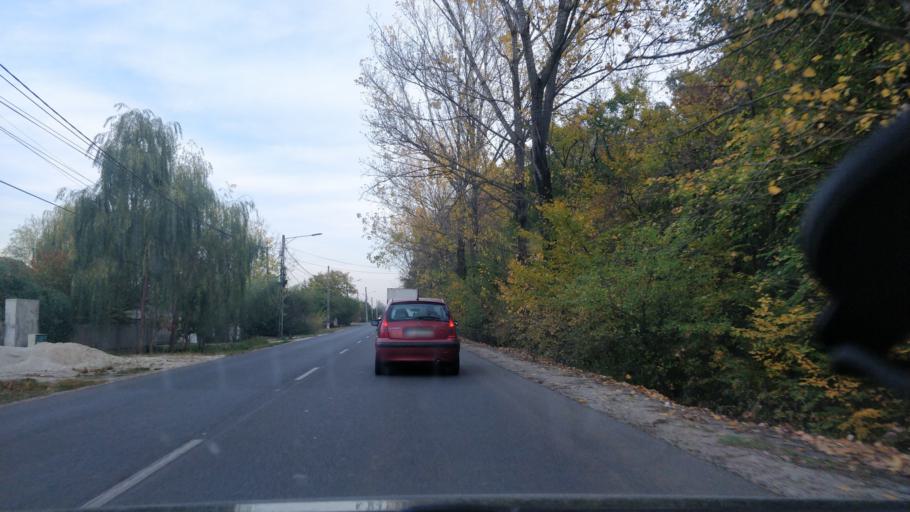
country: RO
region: Ilfov
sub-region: Comuna Ciorogarla
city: Ciorogarla
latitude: 44.4464
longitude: 25.8559
